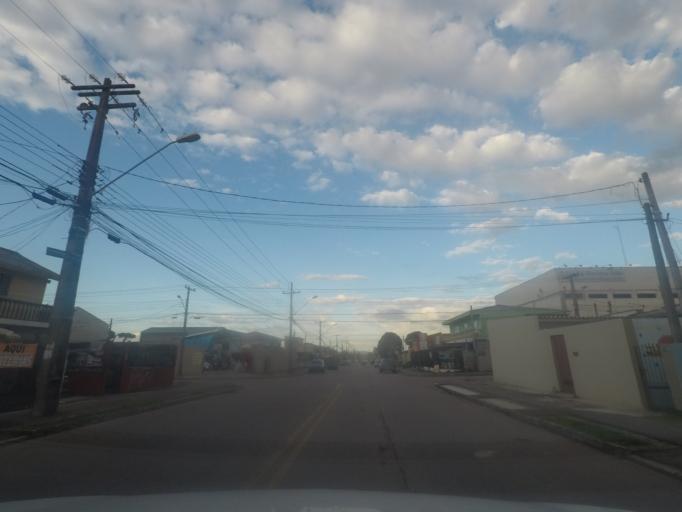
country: BR
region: Parana
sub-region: Pinhais
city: Pinhais
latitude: -25.4664
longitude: -49.2025
